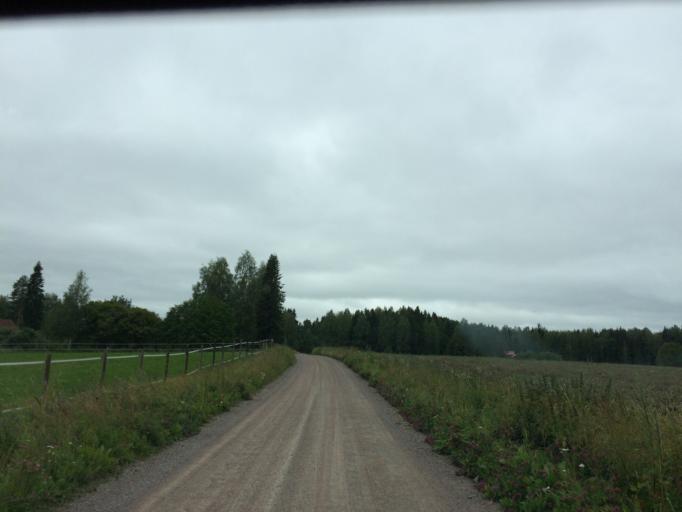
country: FI
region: Haeme
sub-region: Haemeenlinna
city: Janakkala
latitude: 60.8478
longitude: 24.5188
